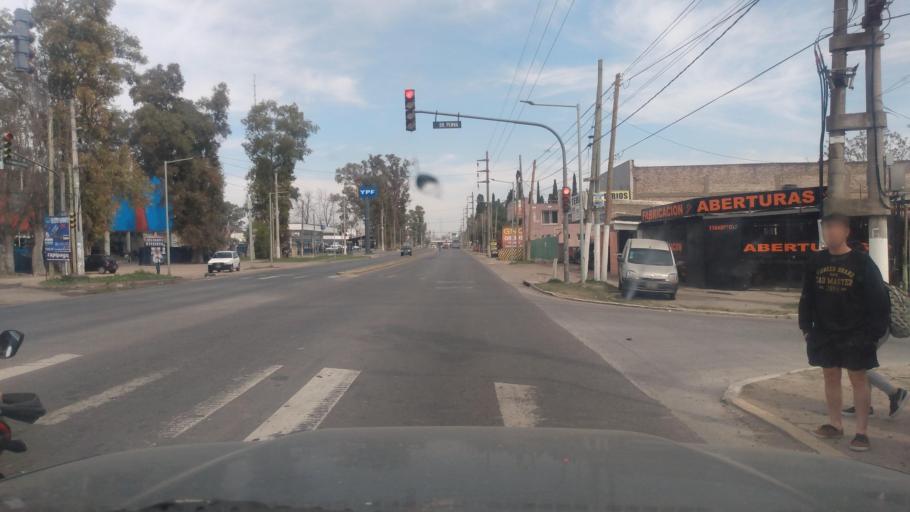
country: AR
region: Buenos Aires
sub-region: Partido de Pilar
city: Pilar
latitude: -34.4454
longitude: -58.9026
